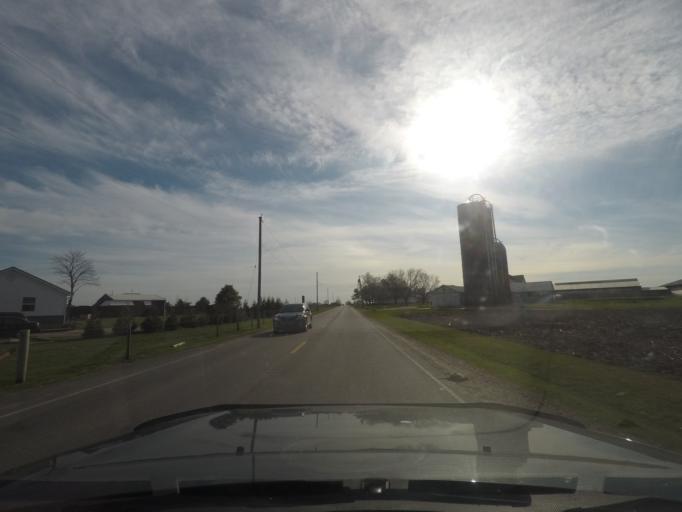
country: US
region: Indiana
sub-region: Elkhart County
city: Wakarusa
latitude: 41.5240
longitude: -85.9631
